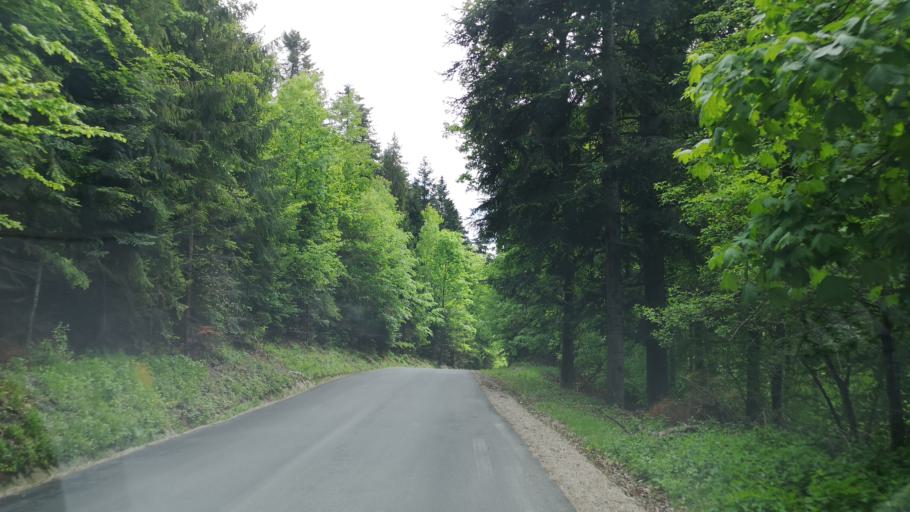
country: SK
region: Banskobystricky
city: Revuca
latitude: 48.6540
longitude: 20.2965
